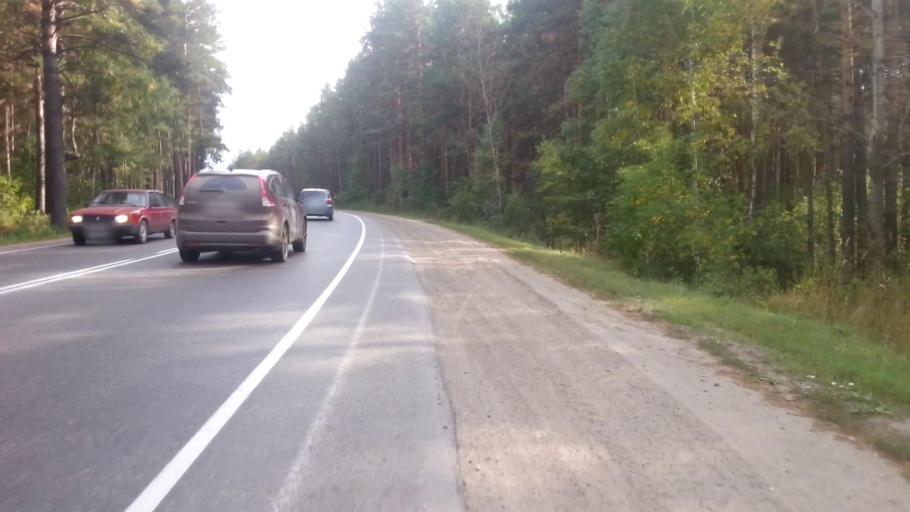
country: RU
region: Altai Krai
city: Yuzhnyy
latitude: 53.2985
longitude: 83.7028
